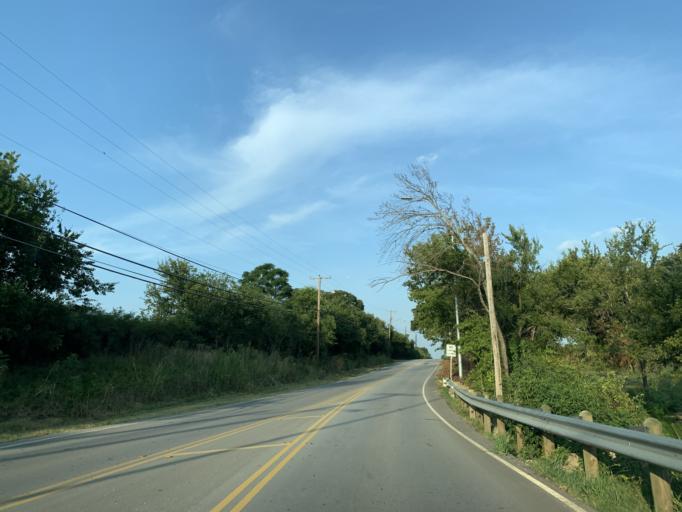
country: US
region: Texas
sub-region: Tarrant County
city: Richland Hills
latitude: 32.7799
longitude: -97.2073
